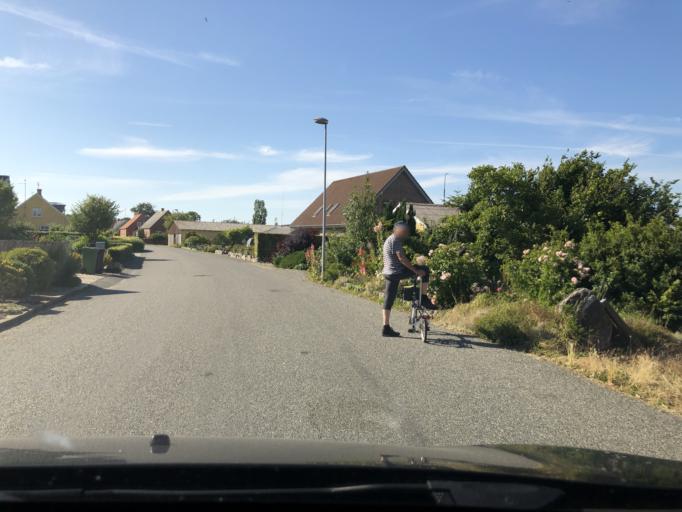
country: DK
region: South Denmark
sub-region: AEro Kommune
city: Marstal
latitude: 54.8707
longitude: 10.4931
